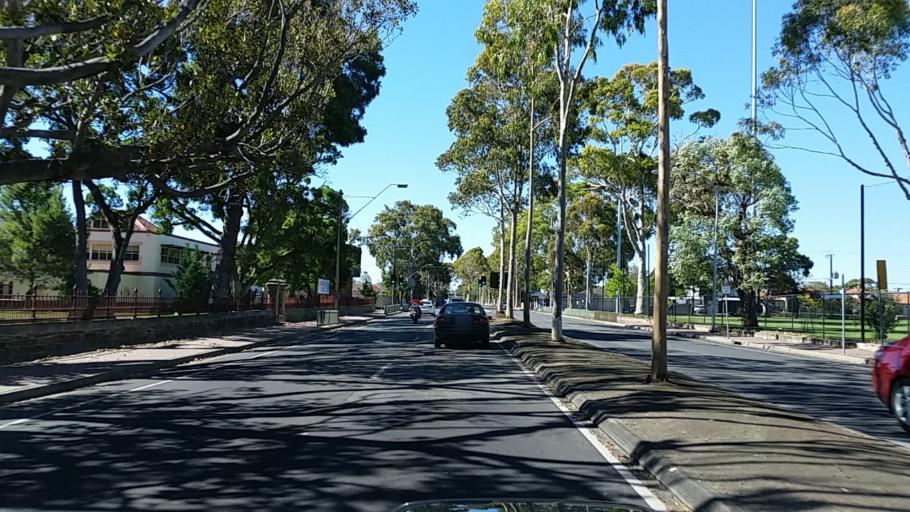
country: AU
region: South Australia
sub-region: Holdfast Bay
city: North Brighton
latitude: -34.9956
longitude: 138.5213
